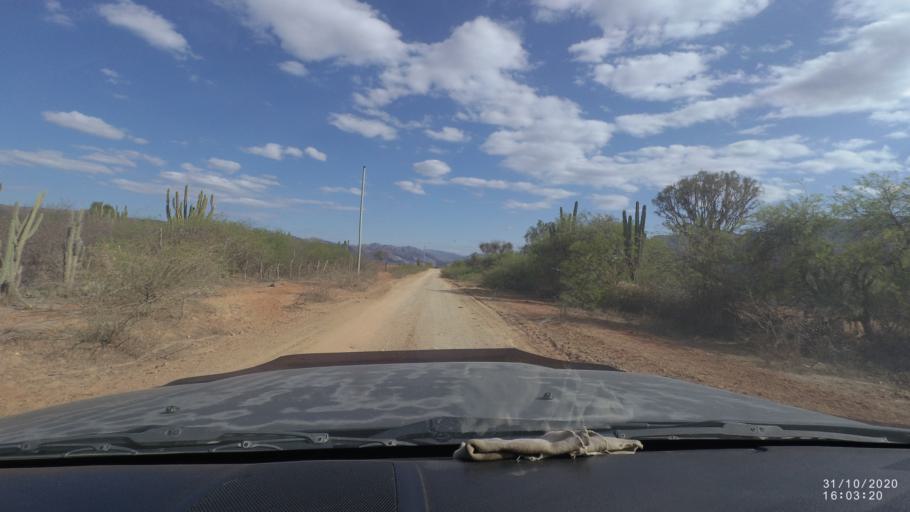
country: BO
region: Chuquisaca
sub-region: Provincia Zudanez
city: Mojocoya
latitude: -18.3511
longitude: -64.6533
